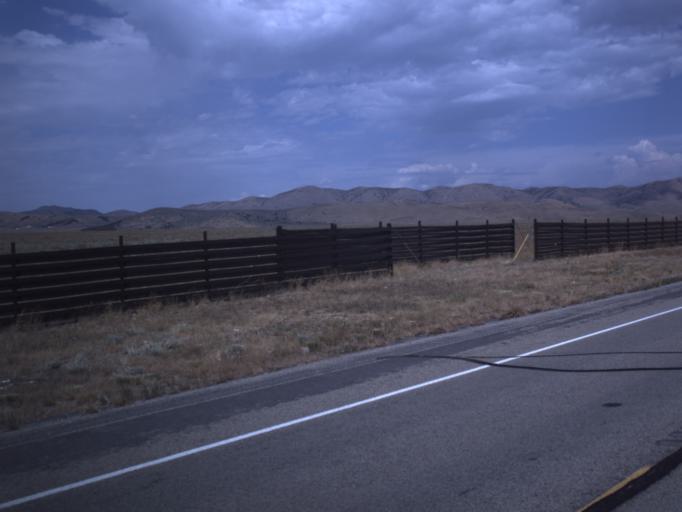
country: US
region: Utah
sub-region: Utah County
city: Eagle Mountain
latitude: 40.3584
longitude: -112.0552
